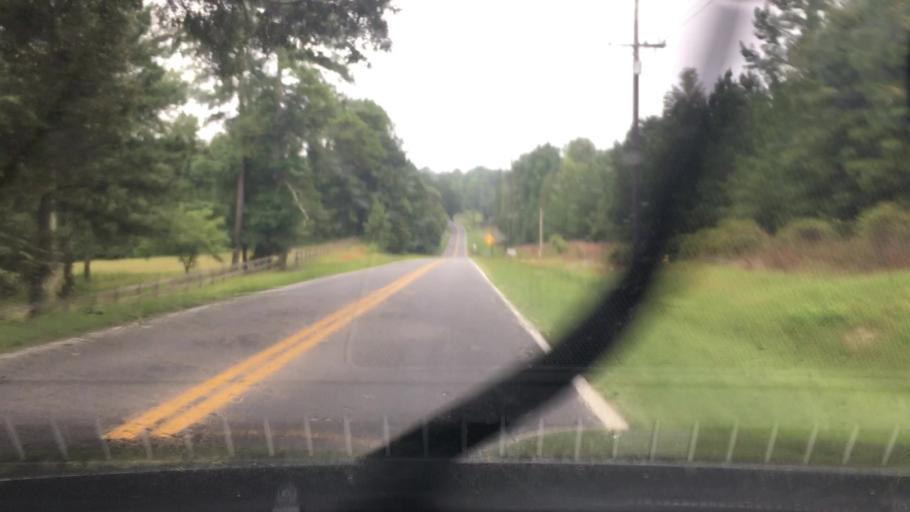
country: US
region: Georgia
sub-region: Spalding County
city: Experiment
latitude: 33.2613
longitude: -84.3876
